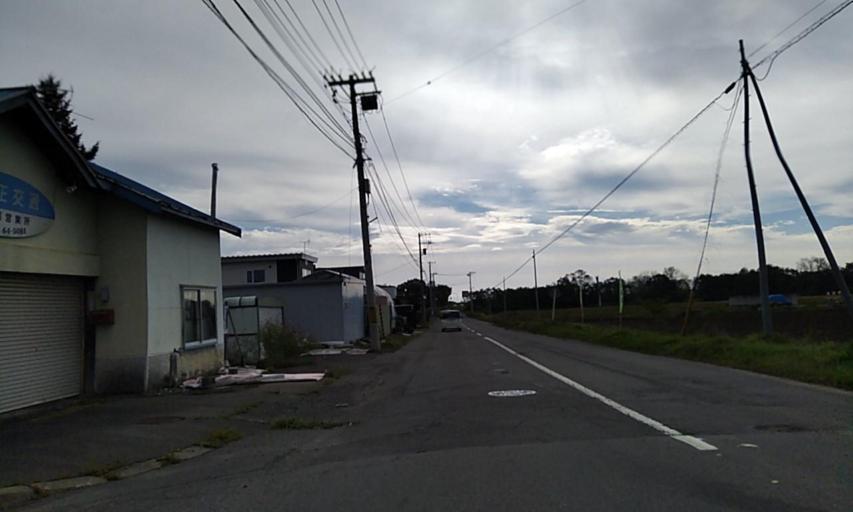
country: JP
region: Hokkaido
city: Obihiro
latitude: 42.8435
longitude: 143.1792
